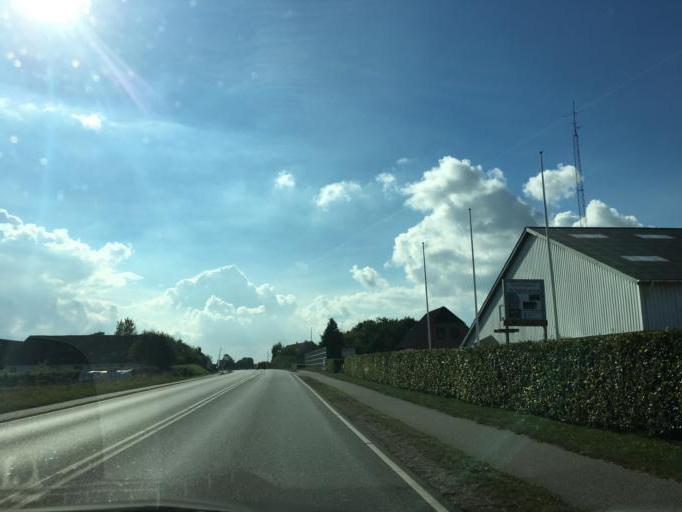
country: DK
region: South Denmark
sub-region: Fredericia Kommune
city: Snoghoj
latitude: 55.5630
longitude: 9.6787
